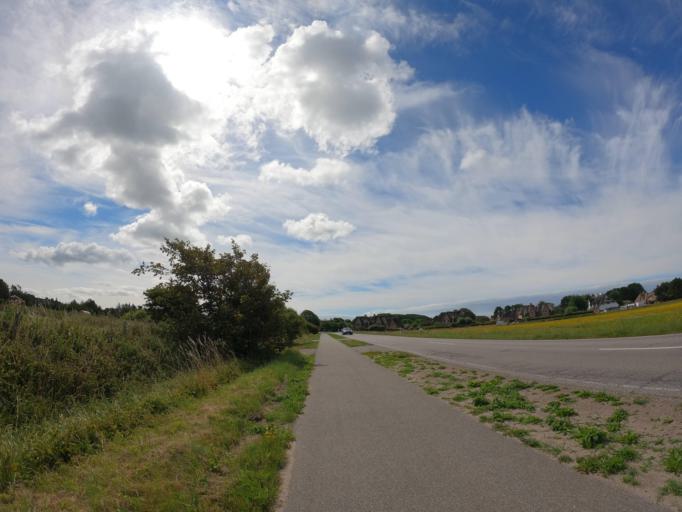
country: DE
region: Schleswig-Holstein
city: Sylt-Ost
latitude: 54.8749
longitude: 8.3921
